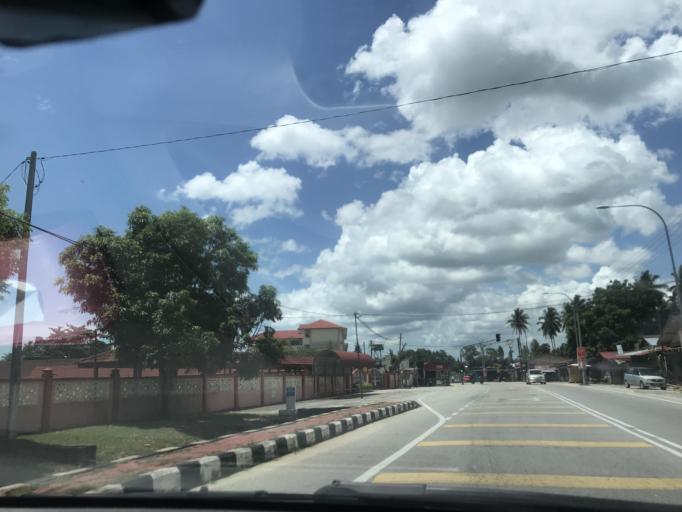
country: MY
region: Kelantan
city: Tumpat
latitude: 6.1884
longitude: 102.1594
